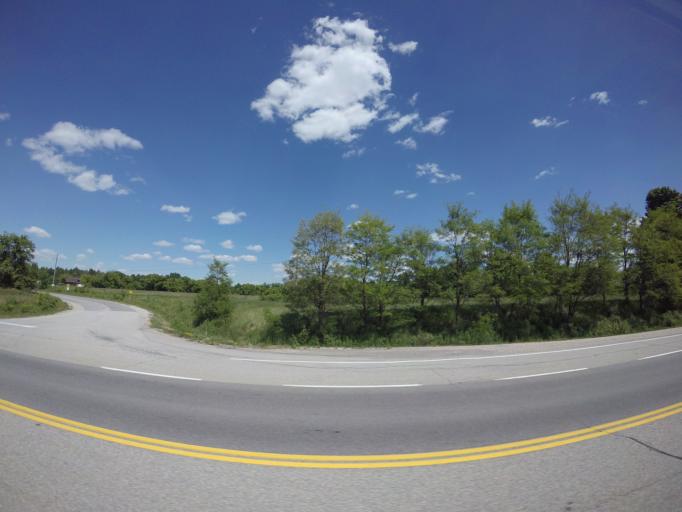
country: CA
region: Ontario
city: Carleton Place
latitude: 45.0467
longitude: -76.2498
